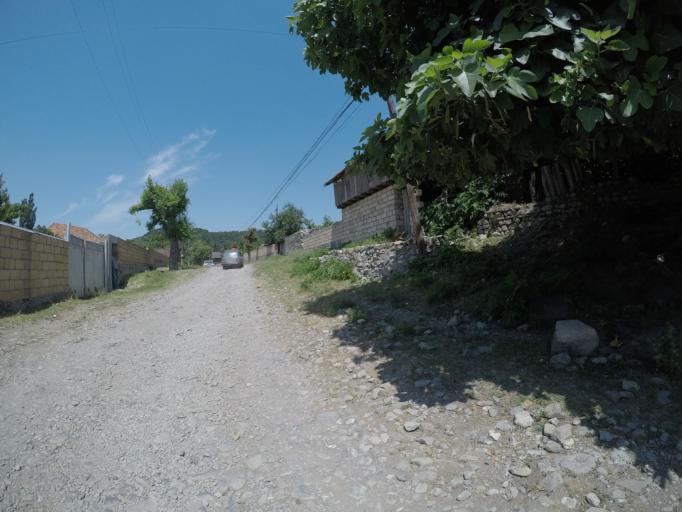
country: AZ
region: Qakh Rayon
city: Cinarli
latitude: 41.4837
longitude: 46.8469
